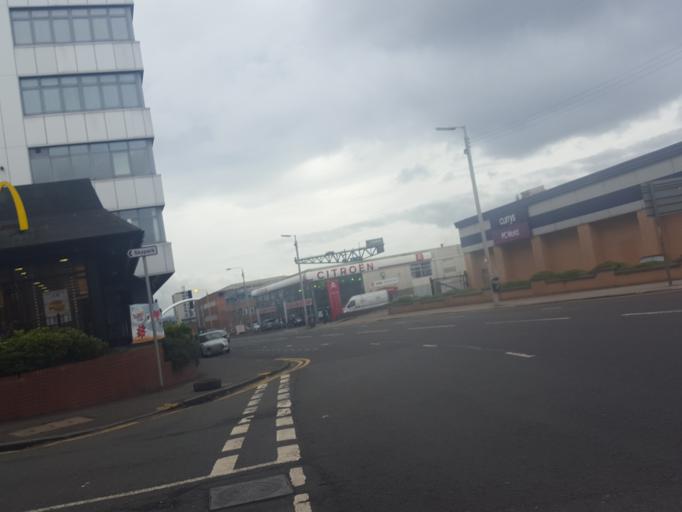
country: GB
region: Scotland
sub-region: Glasgow City
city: Glasgow
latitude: 55.8629
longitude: -4.2803
